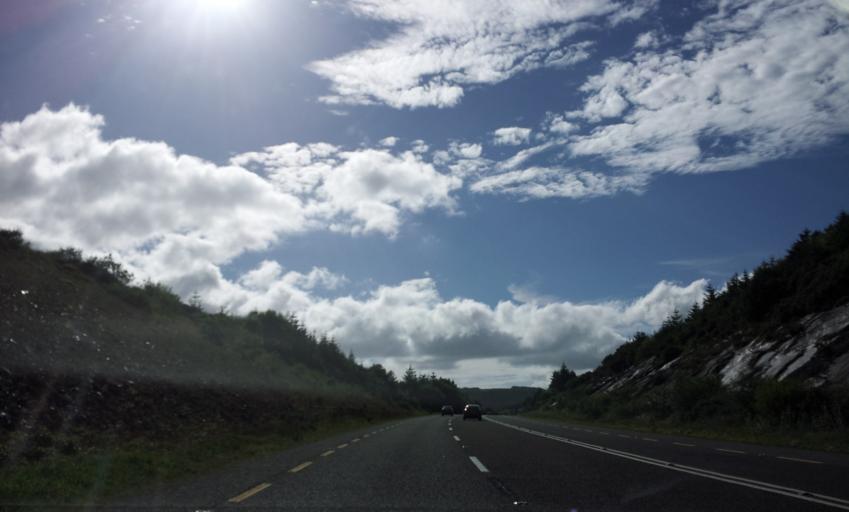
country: IE
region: Munster
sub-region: County Cork
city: Millstreet
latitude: 51.9625
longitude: -9.2151
